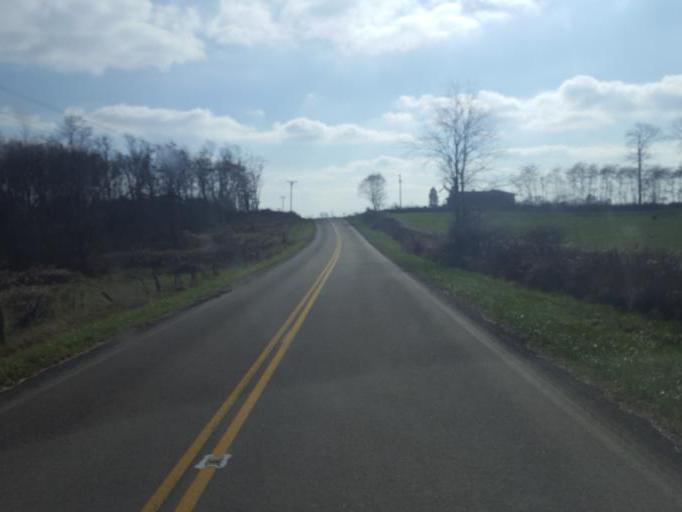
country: US
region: Ohio
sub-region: Knox County
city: Oak Hill
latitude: 40.4346
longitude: -82.1428
